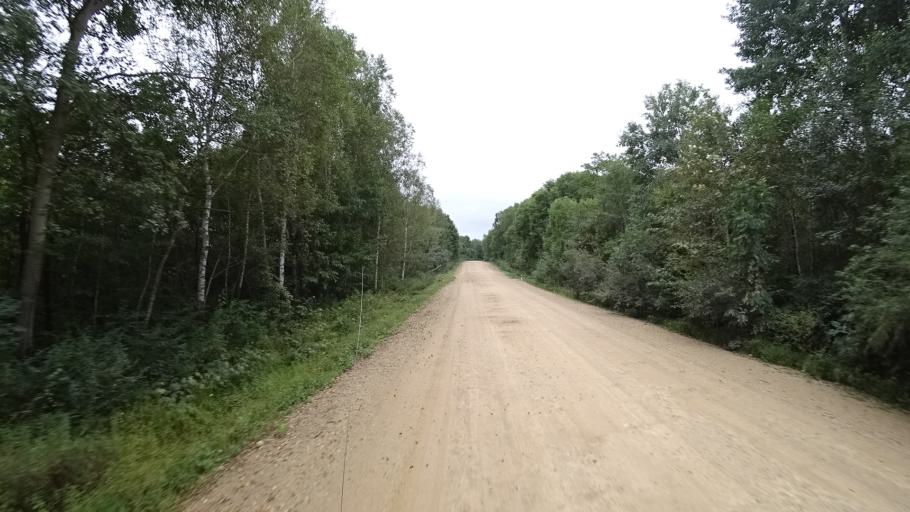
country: RU
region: Primorskiy
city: Rettikhovka
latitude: 44.1634
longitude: 132.7304
